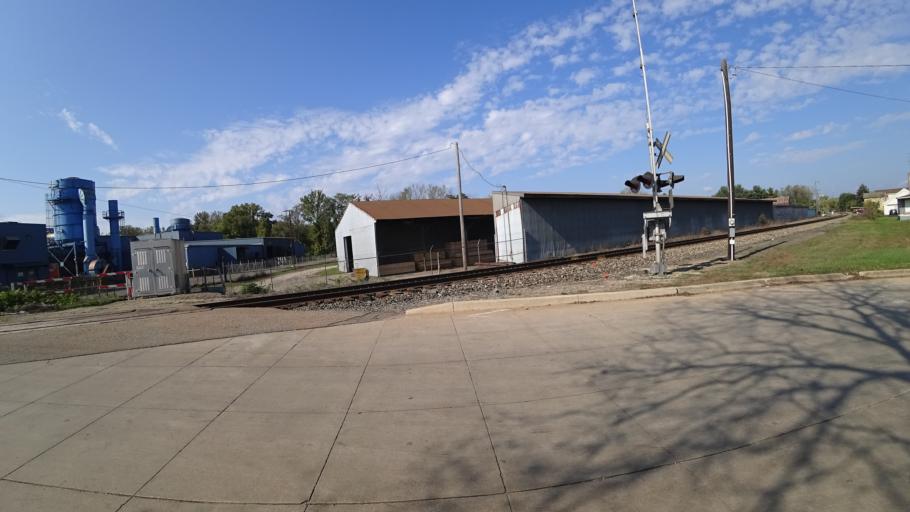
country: US
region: Michigan
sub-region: Saint Joseph County
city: Three Rivers
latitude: 41.9397
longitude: -85.6297
